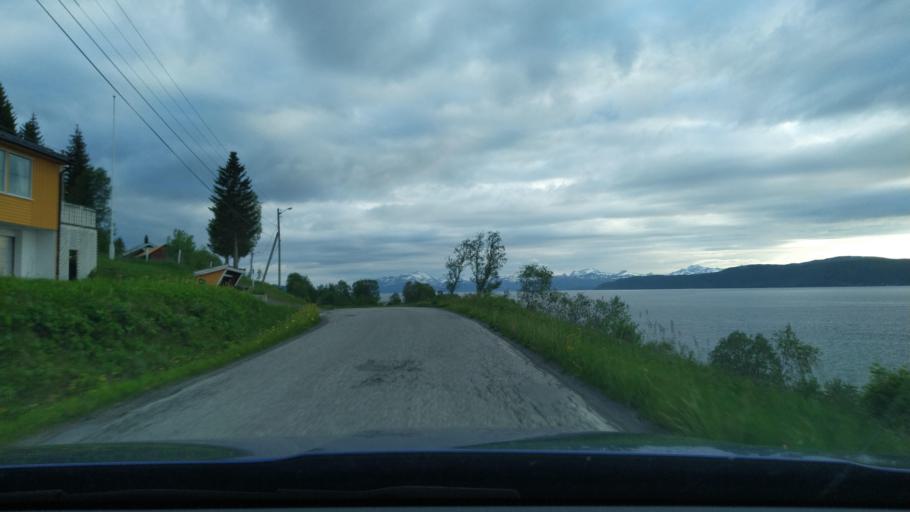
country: NO
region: Troms
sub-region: Lenvik
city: Finnsnes
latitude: 69.1330
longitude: 17.8866
